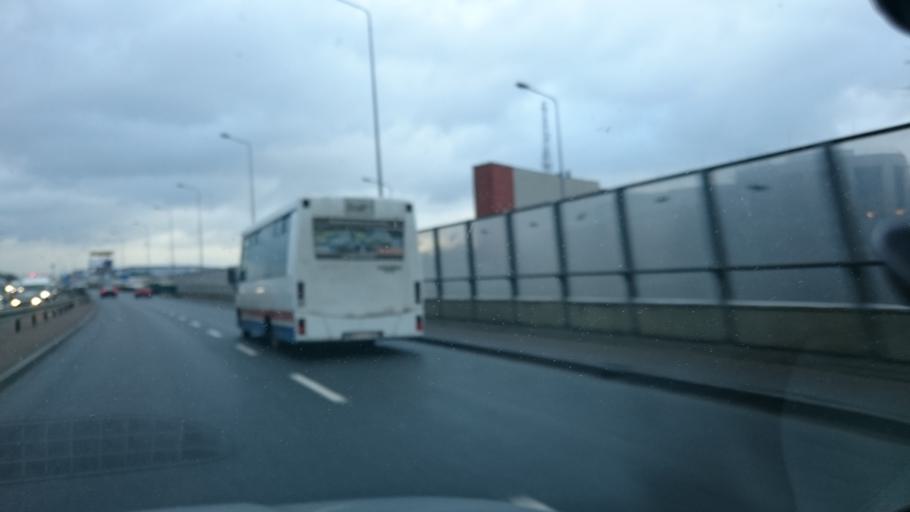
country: PL
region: Lesser Poland Voivodeship
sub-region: Krakow
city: Krakow
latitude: 50.0298
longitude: 19.9525
